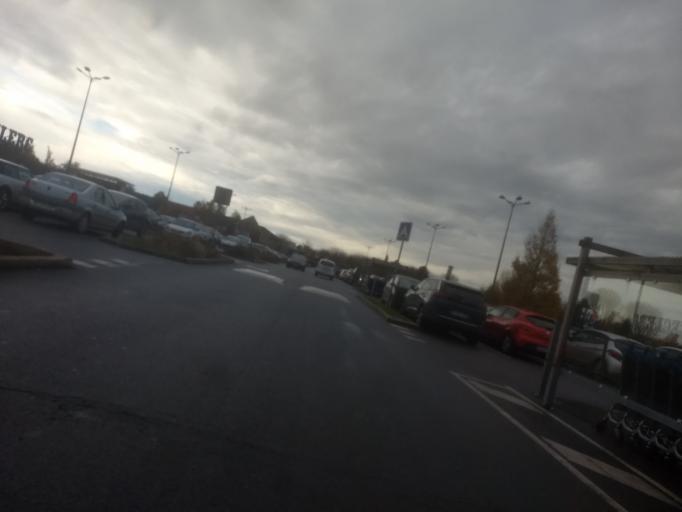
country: FR
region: Nord-Pas-de-Calais
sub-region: Departement du Pas-de-Calais
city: Dainville
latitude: 50.2829
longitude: 2.7398
